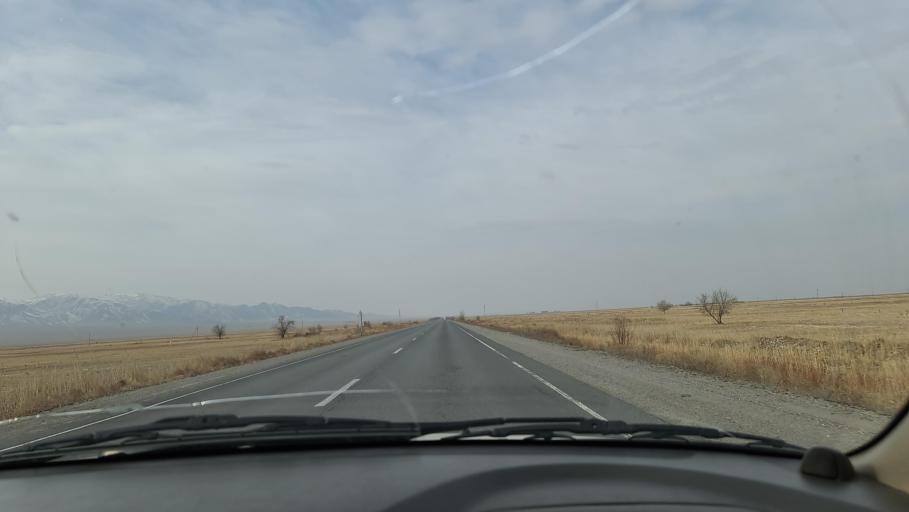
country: KG
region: Chuy
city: Tokmok
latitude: 43.3548
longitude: 75.4373
